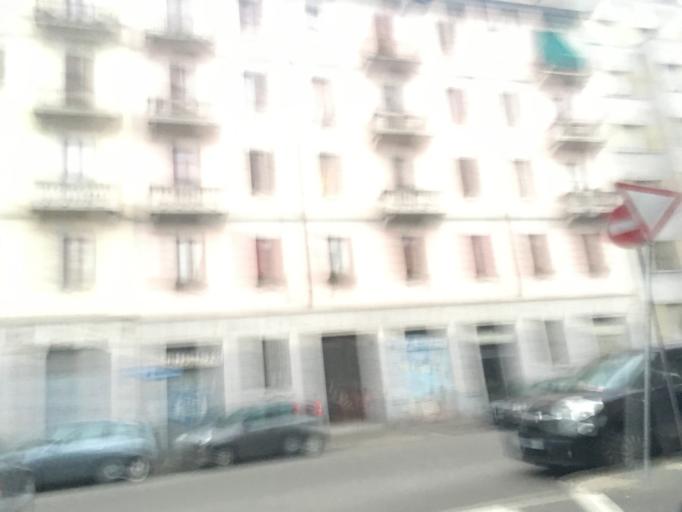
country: IT
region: Lombardy
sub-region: Citta metropolitana di Milano
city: Milano
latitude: 45.4477
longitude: 9.1605
